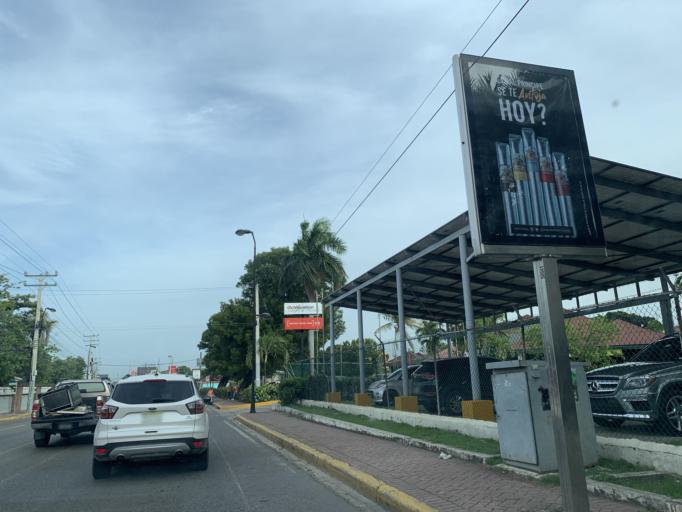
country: DO
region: Puerto Plata
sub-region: Puerto Plata
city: Puerto Plata
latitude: 19.7796
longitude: -70.6702
